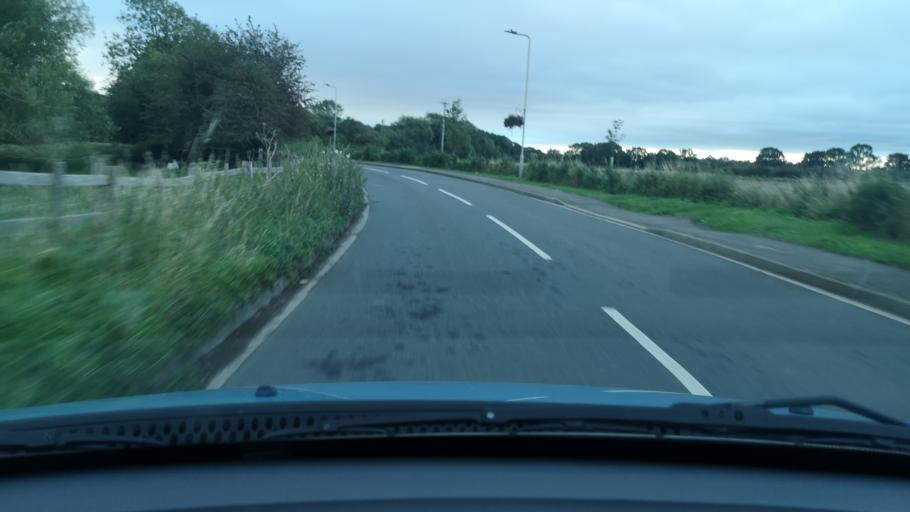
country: GB
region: England
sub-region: Doncaster
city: Norton
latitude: 53.6429
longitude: -1.2085
